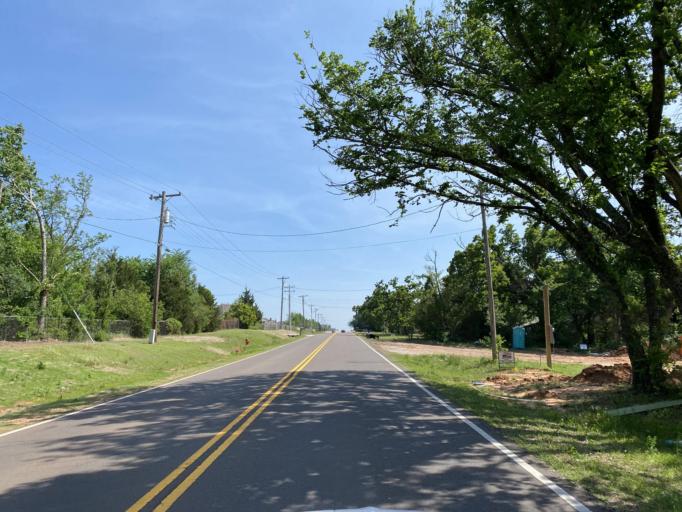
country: US
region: Oklahoma
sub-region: Oklahoma County
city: Nicoma Park
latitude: 35.4687
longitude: -97.3357
